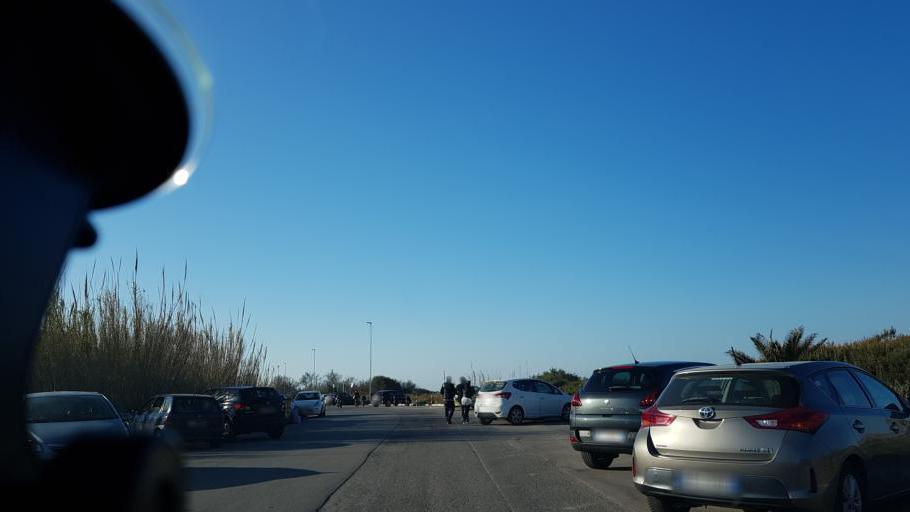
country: IT
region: Apulia
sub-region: Provincia di Lecce
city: Struda
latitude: 40.3918
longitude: 18.3038
